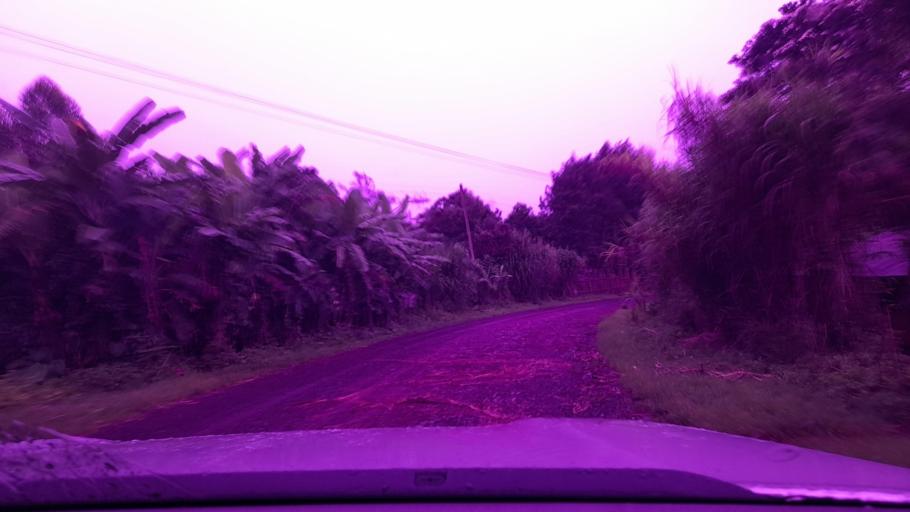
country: ET
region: Oromiya
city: Metu
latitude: 8.4580
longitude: 35.6372
